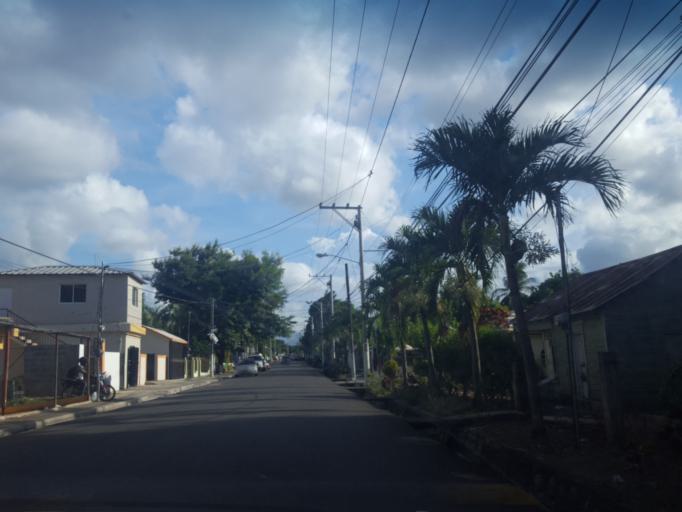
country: DO
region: Santiago
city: Licey al Medio
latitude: 19.3810
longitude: -70.6335
